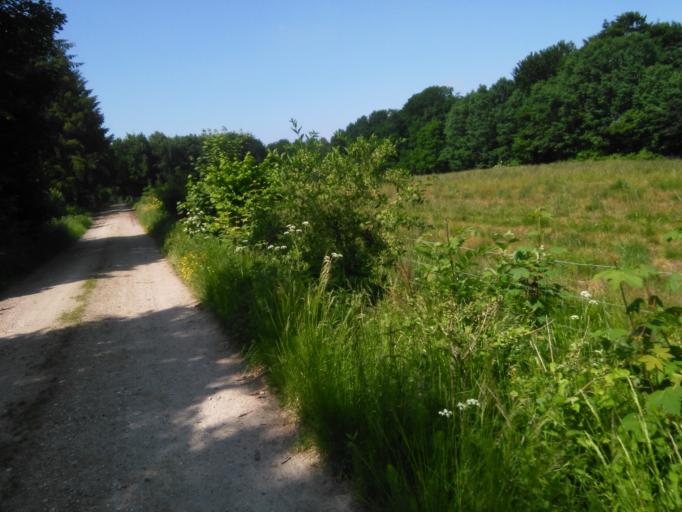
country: DK
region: Central Jutland
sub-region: Odder Kommune
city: Odder
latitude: 55.9555
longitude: 10.0689
